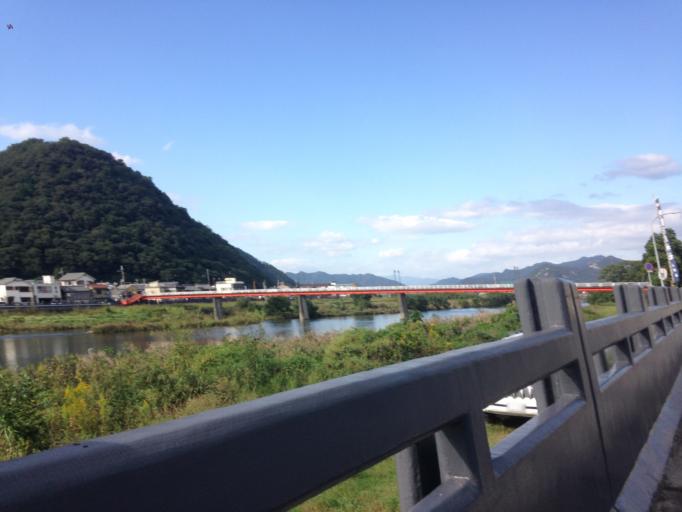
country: JP
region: Hyogo
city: Tatsunocho-tominaga
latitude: 34.8652
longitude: 134.5498
